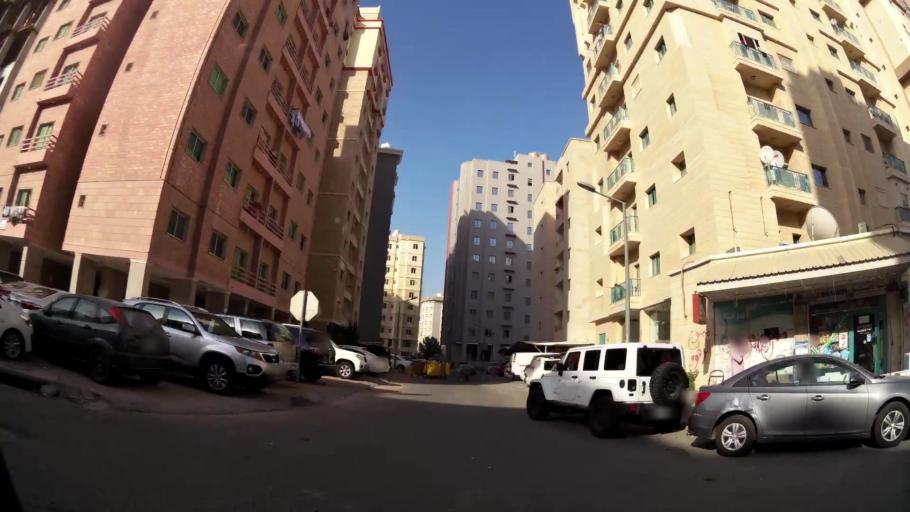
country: KW
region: Muhafazat Hawalli
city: As Salimiyah
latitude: 29.3411
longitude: 48.0928
